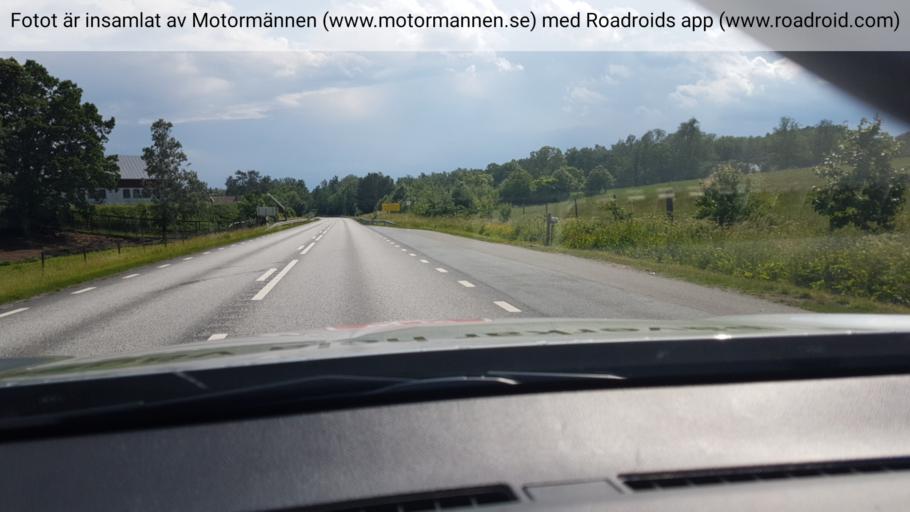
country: SE
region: Joenkoeping
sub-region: Habo Kommun
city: Habo
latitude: 58.0846
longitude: 14.1970
